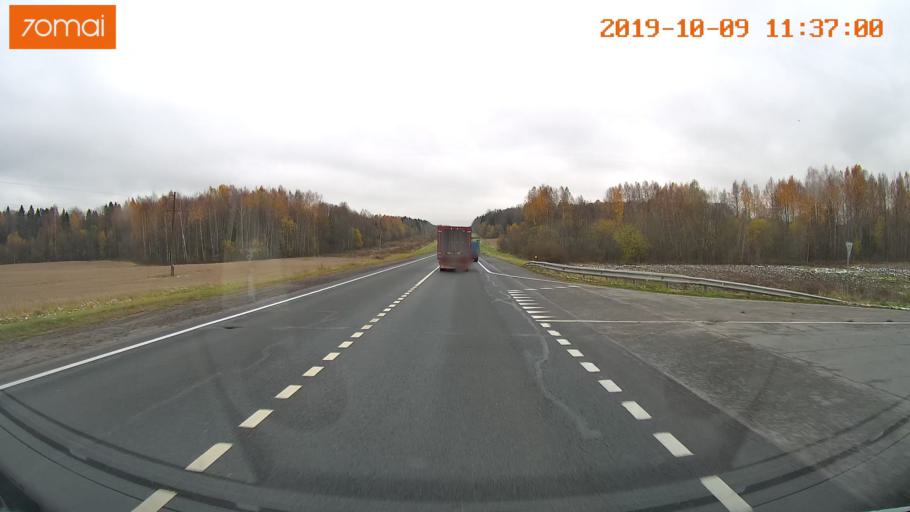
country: RU
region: Vologda
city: Gryazovets
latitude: 58.9838
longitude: 40.1419
